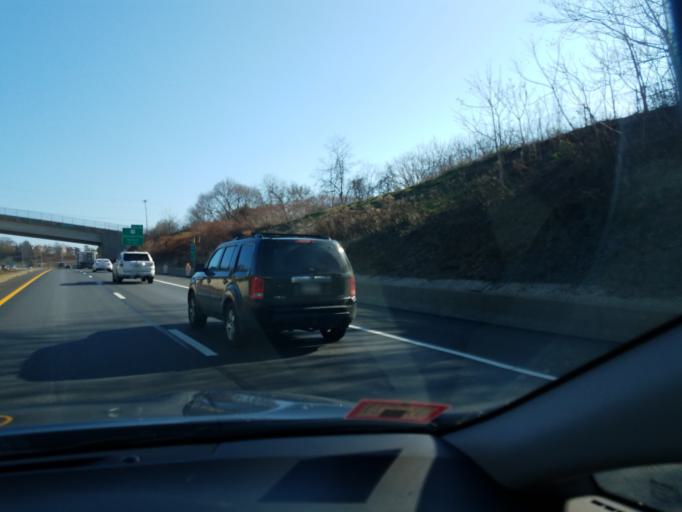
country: US
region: Pennsylvania
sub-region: Allegheny County
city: West View
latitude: 40.5072
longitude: -80.0393
